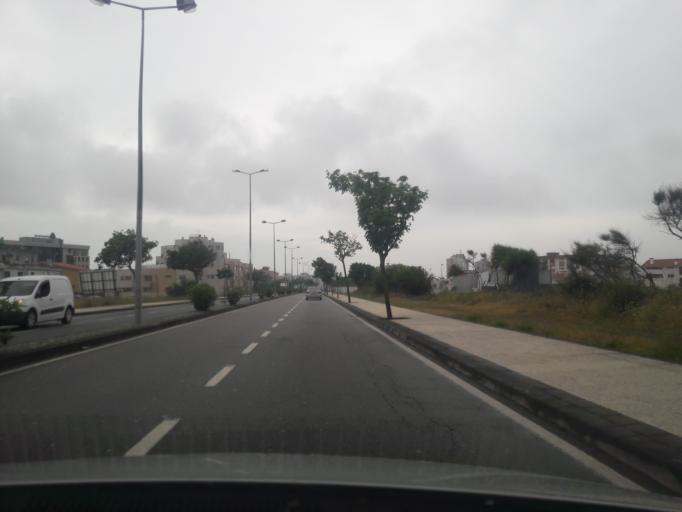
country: PT
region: Porto
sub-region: Povoa de Varzim
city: Povoa de Varzim
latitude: 41.3924
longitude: -8.7590
